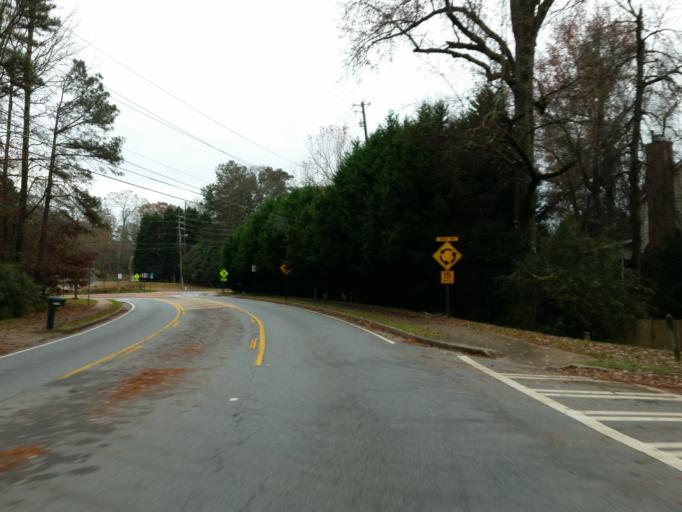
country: US
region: Georgia
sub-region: Cherokee County
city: Woodstock
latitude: 34.0277
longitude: -84.4683
